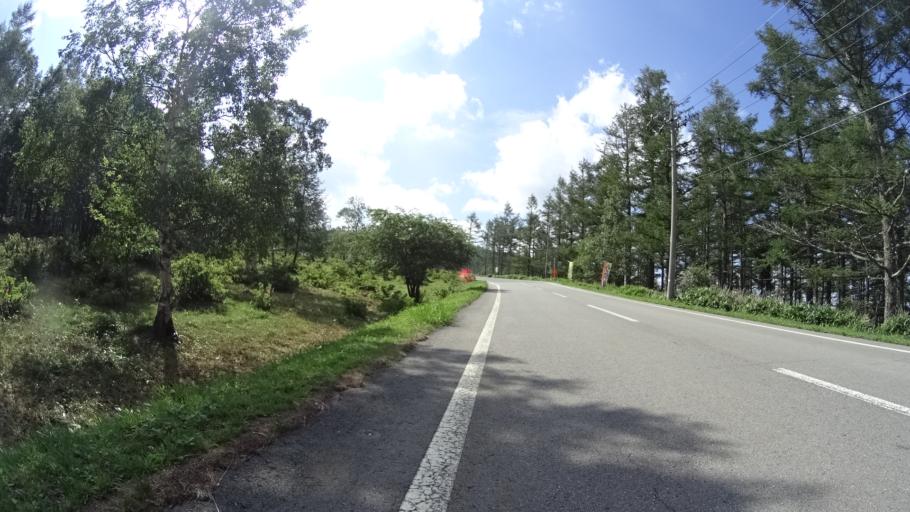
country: JP
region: Nagano
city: Saku
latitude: 36.0639
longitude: 138.3949
